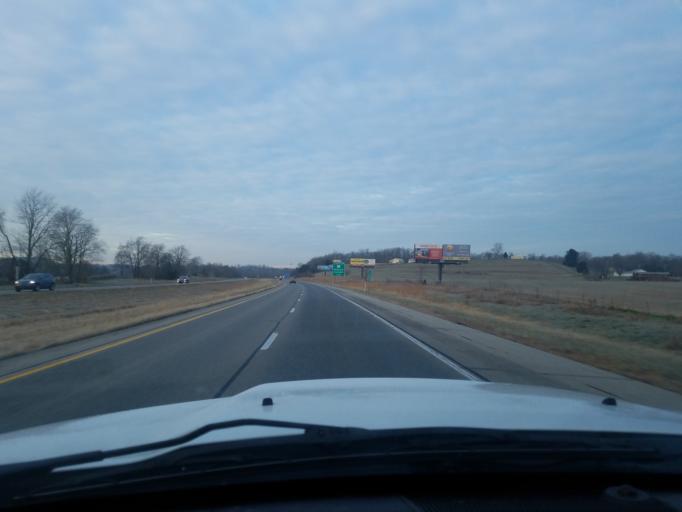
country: US
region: Indiana
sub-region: Harrison County
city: Corydon
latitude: 38.2430
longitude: -86.1066
